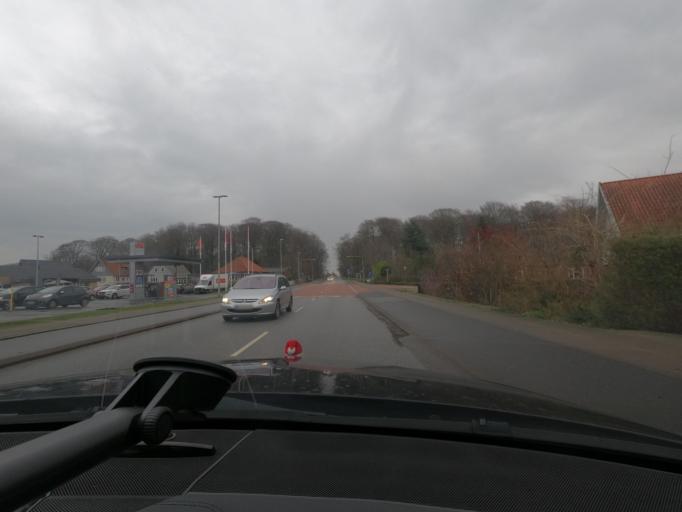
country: DK
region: South Denmark
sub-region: Sonderborg Kommune
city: Horuphav
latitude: 54.9106
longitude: 9.8931
